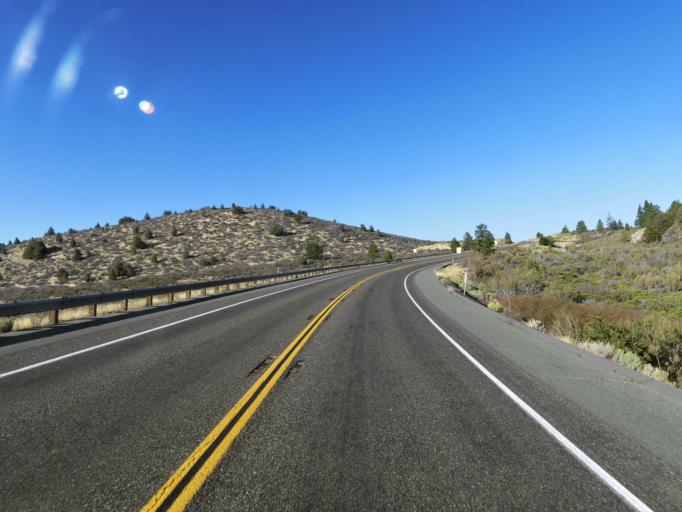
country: US
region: California
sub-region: Siskiyou County
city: Weed
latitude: 41.4769
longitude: -122.3499
